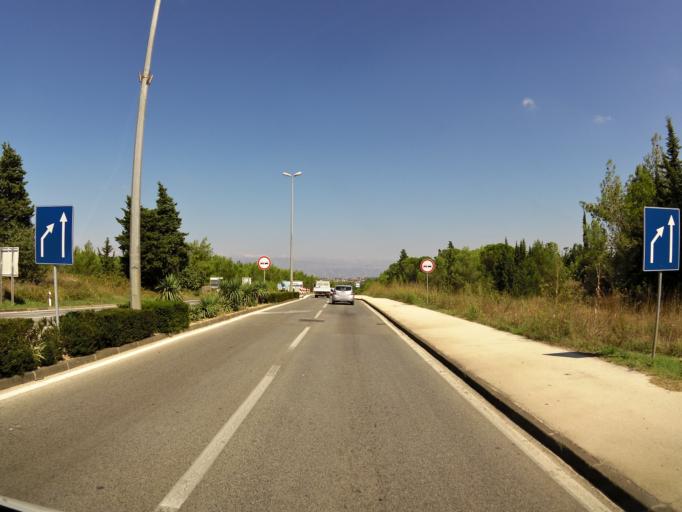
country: HR
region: Zadarska
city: Zadar
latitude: 44.1237
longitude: 15.2809
